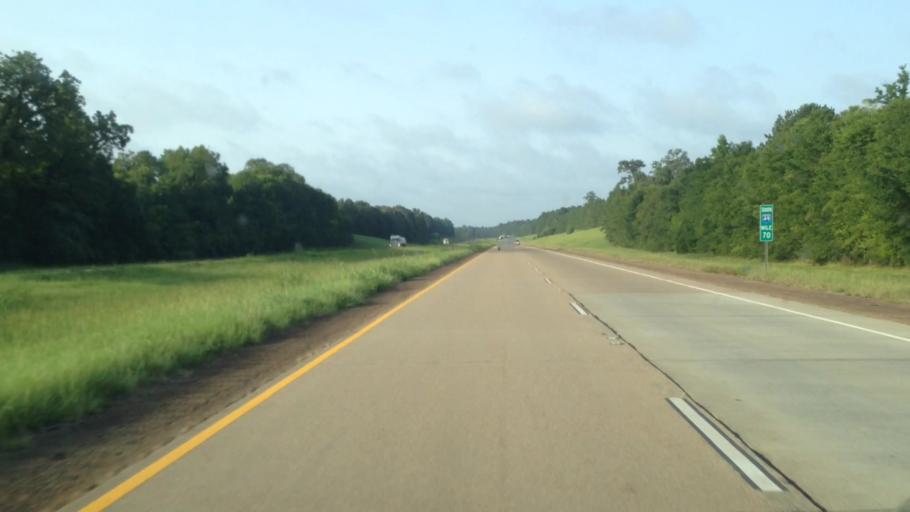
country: US
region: Louisiana
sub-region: Rapides Parish
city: Lecompte
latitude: 31.1162
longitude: -92.4431
